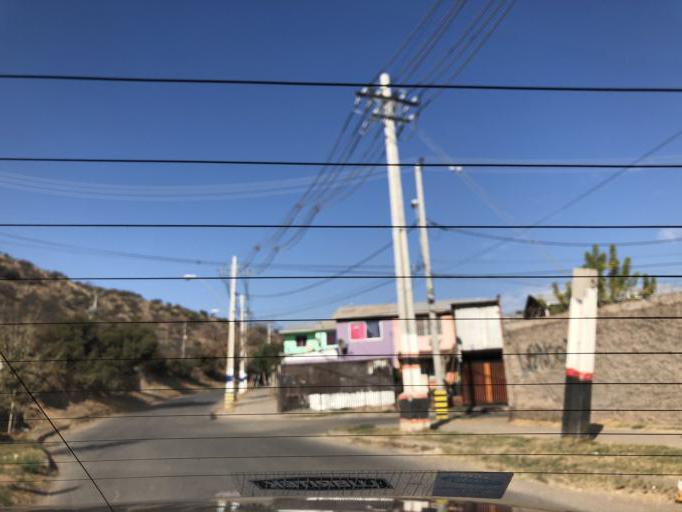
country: CL
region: Santiago Metropolitan
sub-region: Provincia de Cordillera
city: Puente Alto
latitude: -33.6240
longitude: -70.6055
